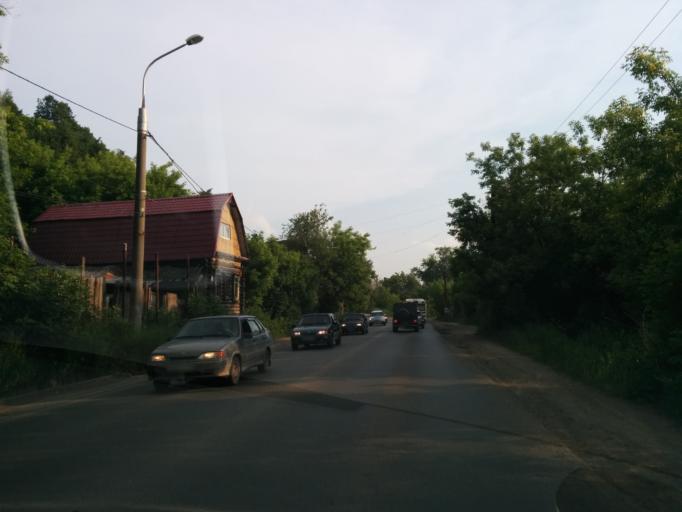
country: RU
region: Perm
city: Perm
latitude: 58.0422
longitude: 56.3187
